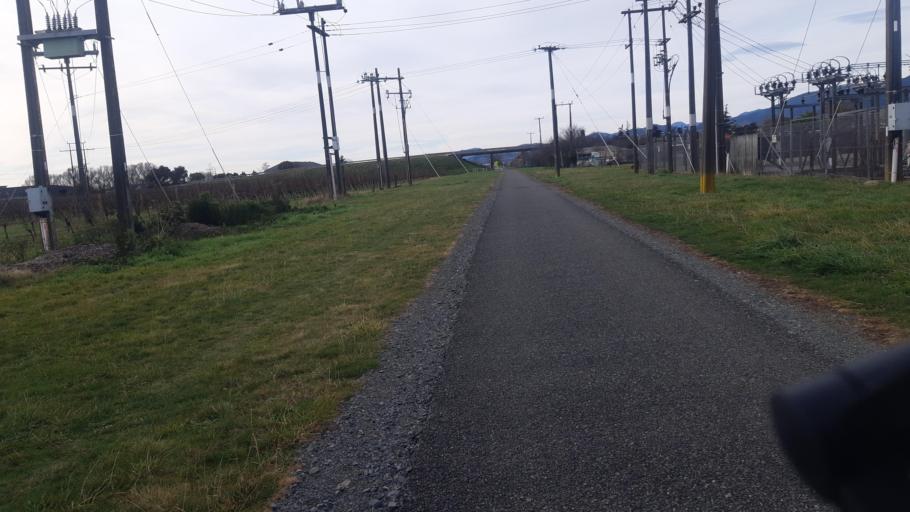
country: NZ
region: Tasman
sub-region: Tasman District
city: Richmond
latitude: -41.3451
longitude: 173.1642
